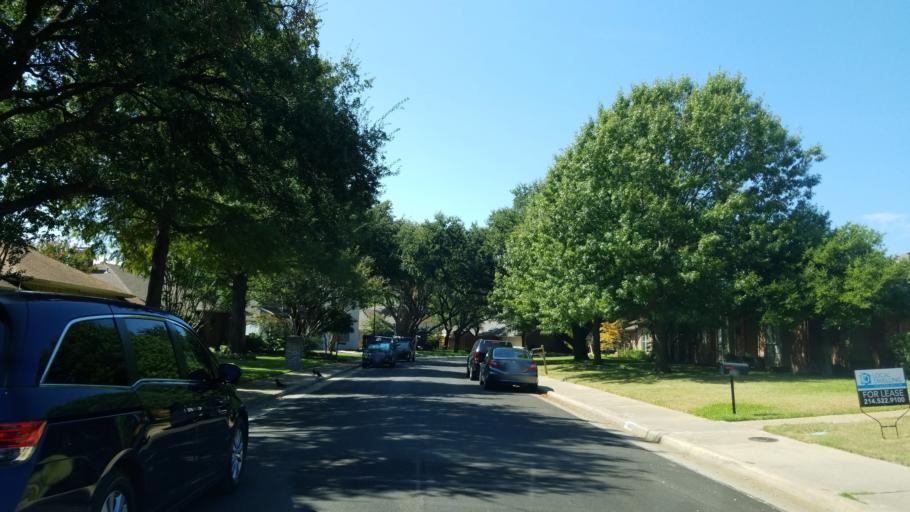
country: US
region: Texas
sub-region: Dallas County
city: Addison
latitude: 32.9703
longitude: -96.7884
